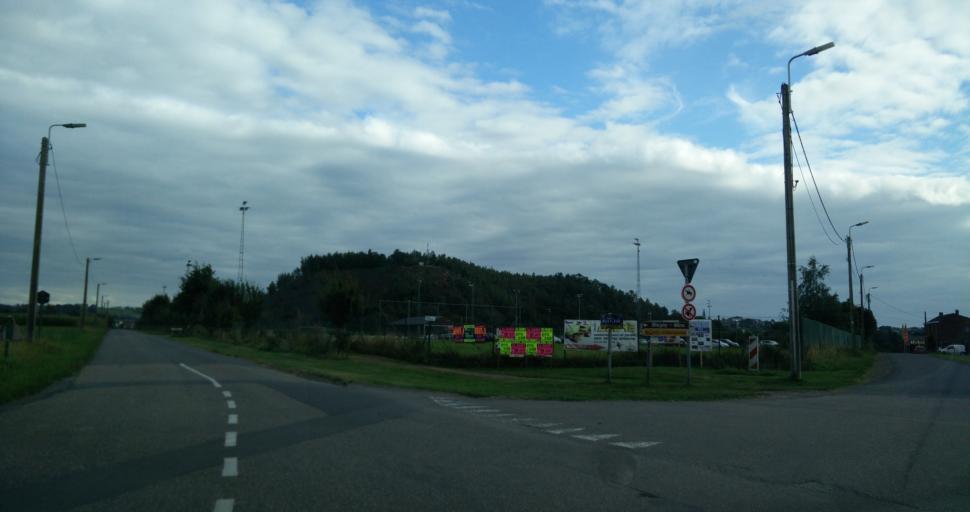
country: BE
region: Wallonia
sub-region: Province de Liege
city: Blegny
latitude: 50.6925
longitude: 5.7175
